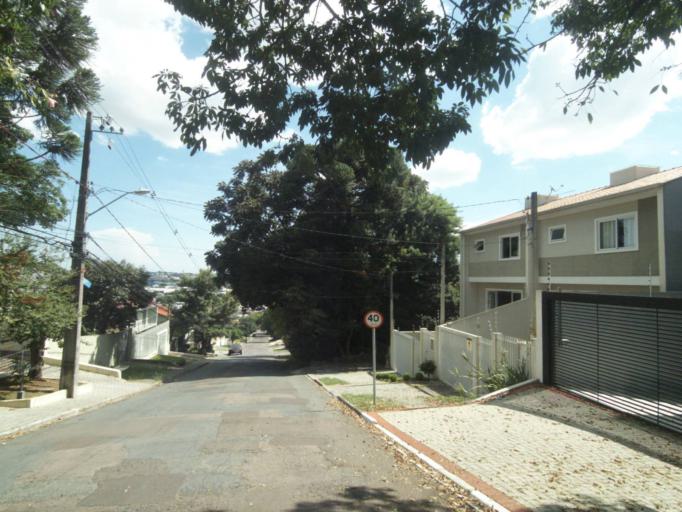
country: BR
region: Parana
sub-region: Curitiba
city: Curitiba
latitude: -25.4711
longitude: -49.2412
